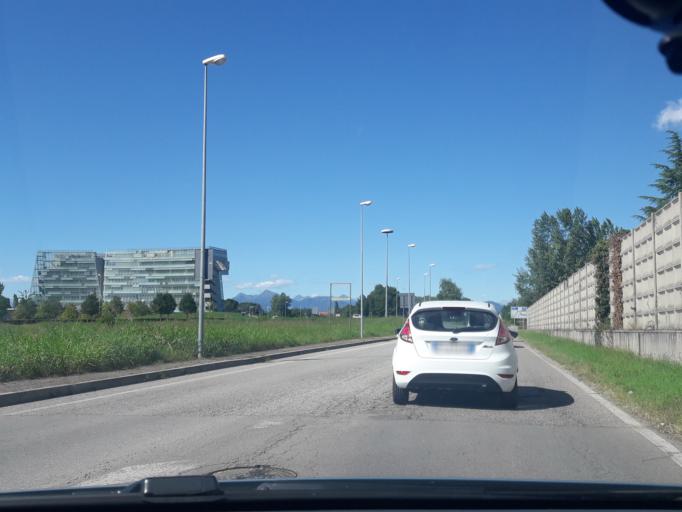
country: IT
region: Friuli Venezia Giulia
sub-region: Provincia di Udine
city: Tavagnacco
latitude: 46.1103
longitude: 13.2181
